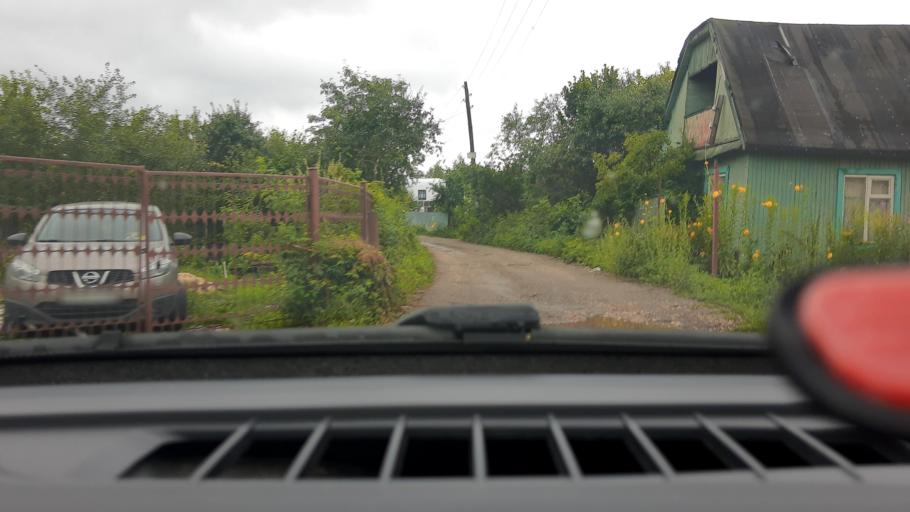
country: RU
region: Nizjnij Novgorod
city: Gorbatovka
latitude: 56.3174
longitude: 43.8363
